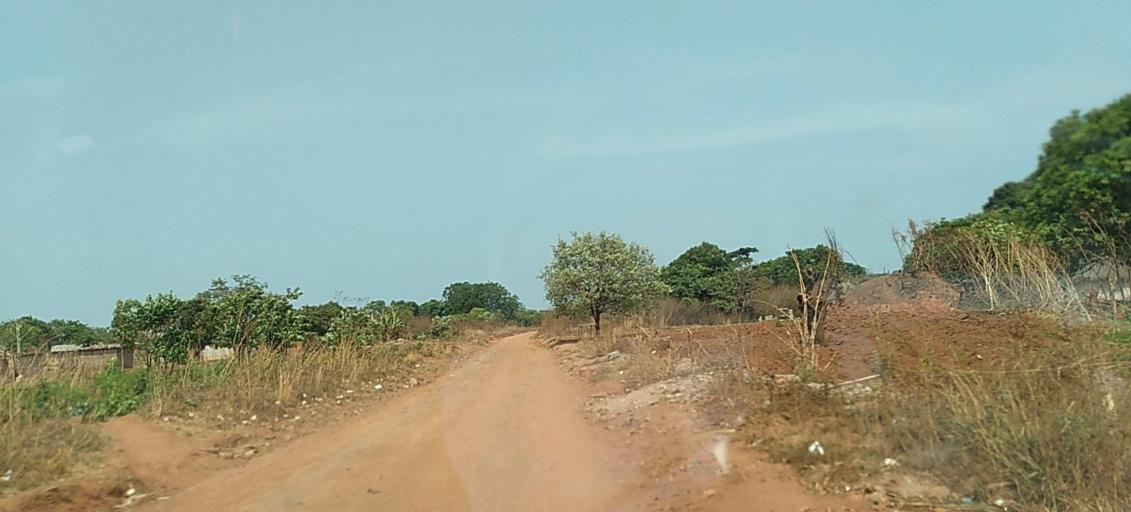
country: ZM
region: Copperbelt
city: Chililabombwe
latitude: -12.3419
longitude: 27.7085
